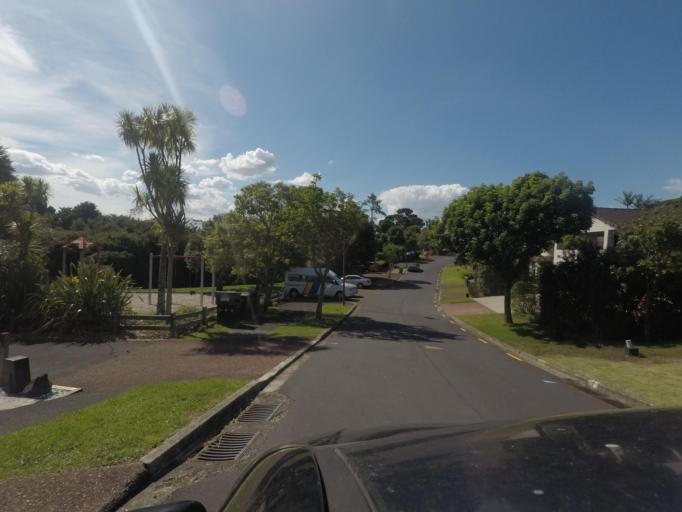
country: NZ
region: Auckland
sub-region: Auckland
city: Waitakere
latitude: -36.9270
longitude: 174.6567
